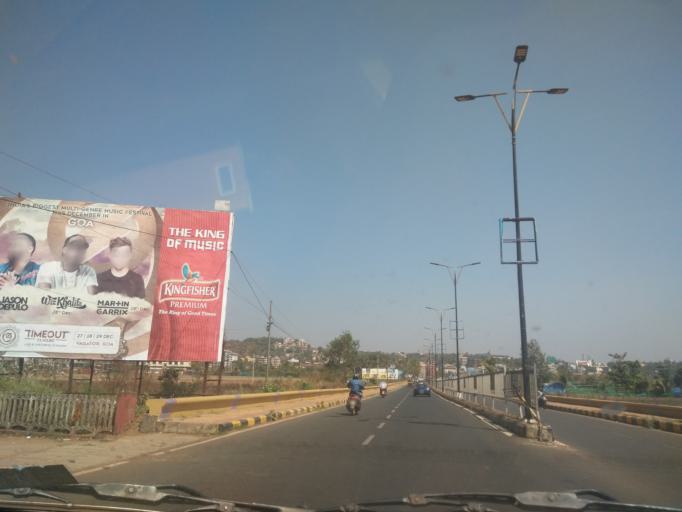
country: IN
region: Goa
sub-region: North Goa
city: Guirim
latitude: 15.5831
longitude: 73.8070
